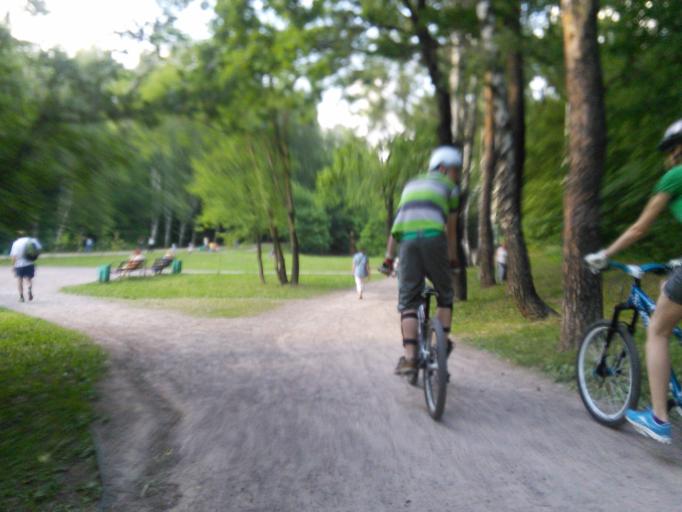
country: RU
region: Moscow
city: Sokol'niki
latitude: 55.8146
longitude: 37.6732
